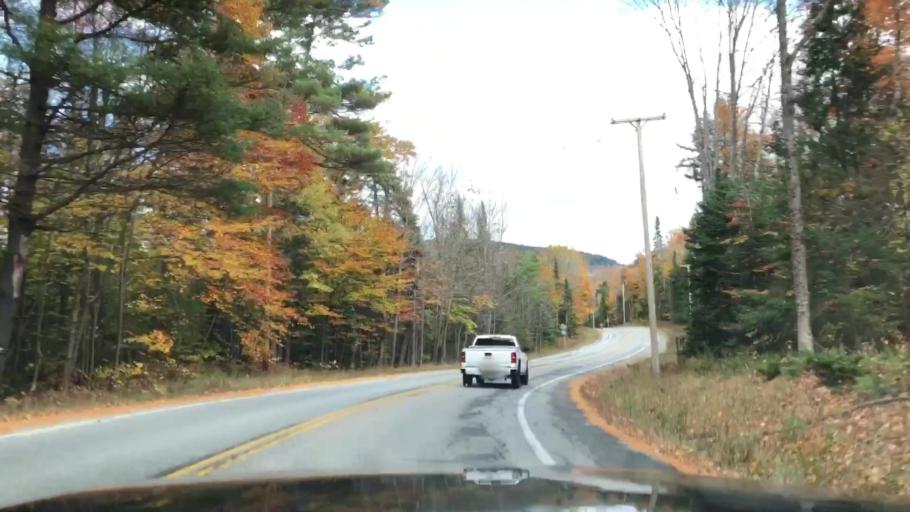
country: US
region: New York
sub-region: Essex County
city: Lake Placid
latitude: 43.8644
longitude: -74.0046
